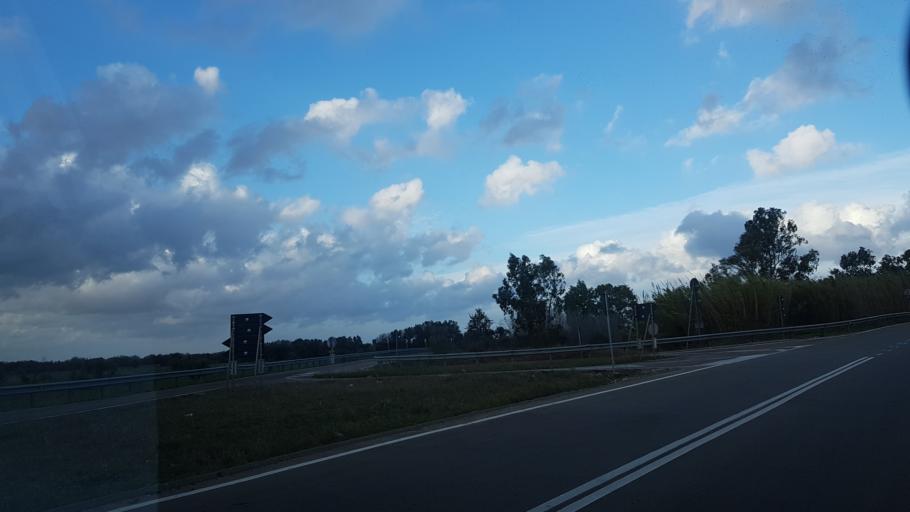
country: IT
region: Apulia
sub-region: Provincia di Brindisi
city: San Pietro Vernotico
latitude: 40.5195
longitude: 18.0147
